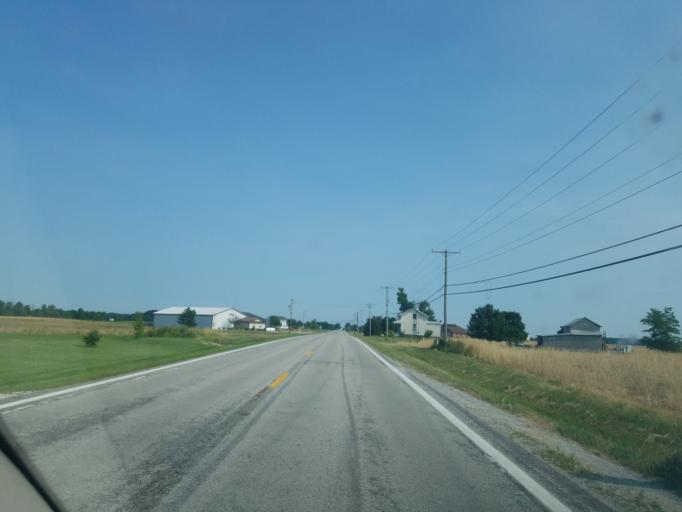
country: US
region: Ohio
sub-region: Wyandot County
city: Carey
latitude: 41.0454
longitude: -83.3128
